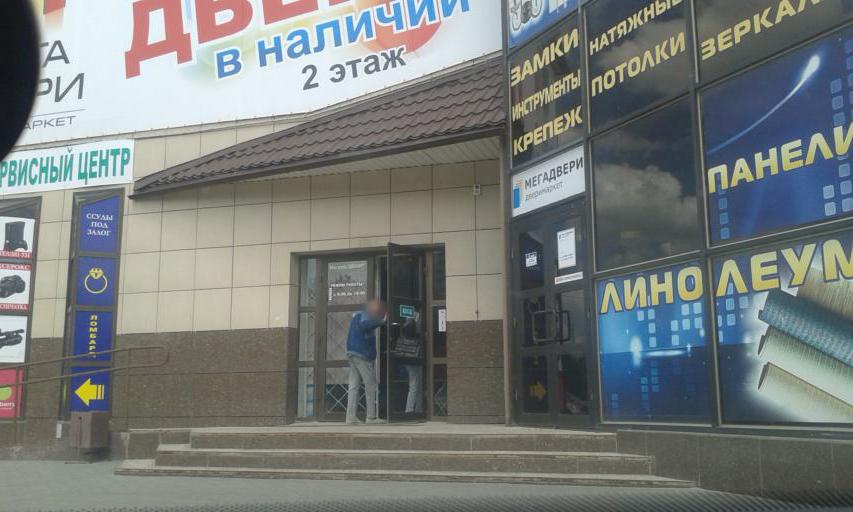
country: RU
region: Volgograd
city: Volgograd
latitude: 48.7581
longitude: 44.5013
